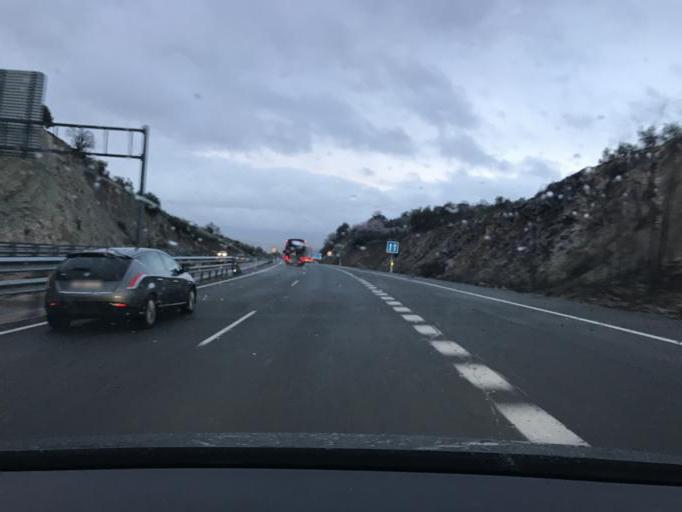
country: ES
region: Andalusia
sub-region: Provincia de Granada
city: Campotejar
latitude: 37.4670
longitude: -3.5687
